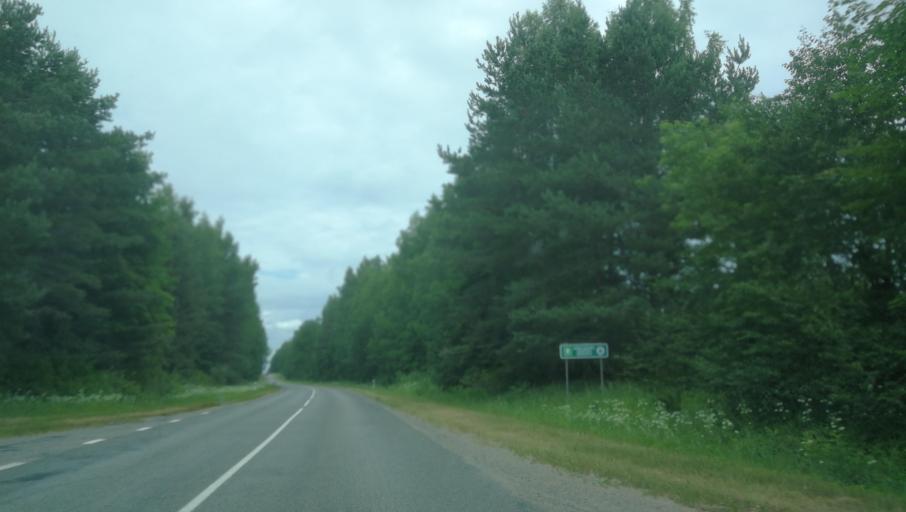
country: LV
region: Valmieras Rajons
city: Valmiera
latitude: 57.6893
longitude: 25.4300
